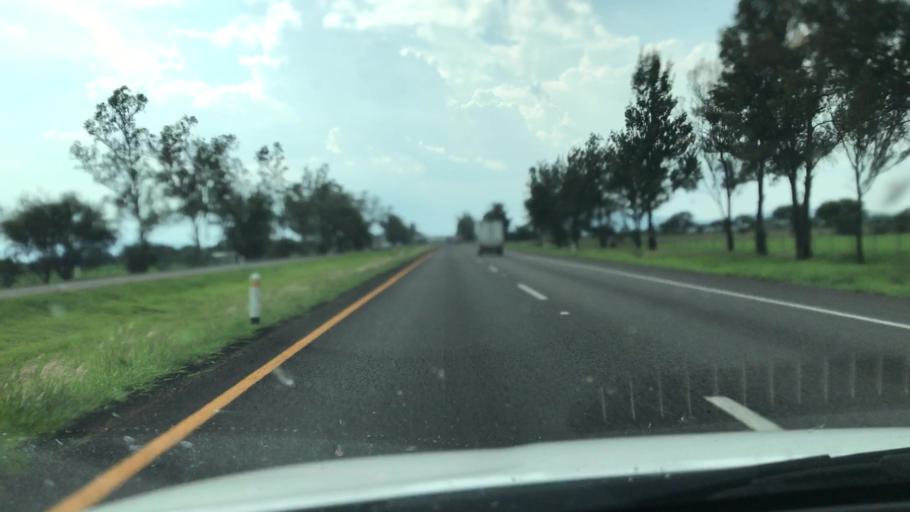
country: MX
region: Jalisco
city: Jamay
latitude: 20.3643
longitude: -102.6490
